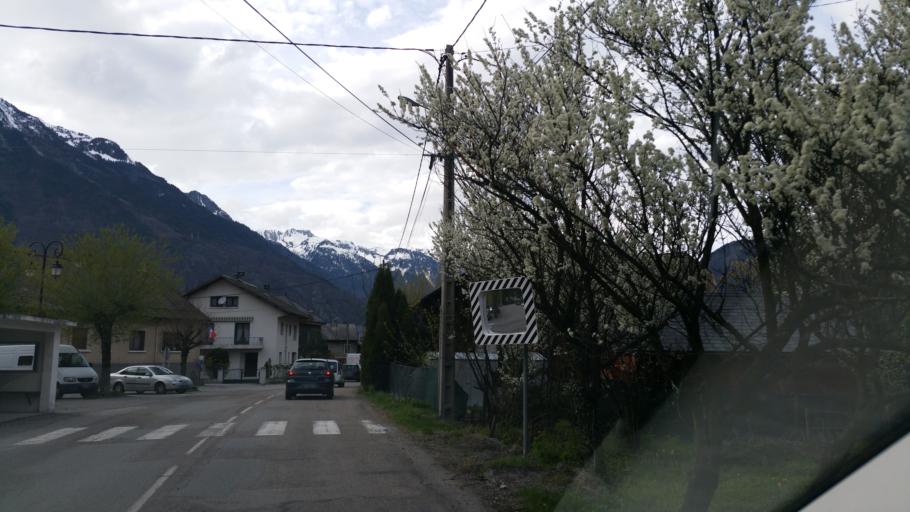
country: FR
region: Rhone-Alpes
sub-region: Departement de la Savoie
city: La Chambre
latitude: 45.3312
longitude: 6.3119
